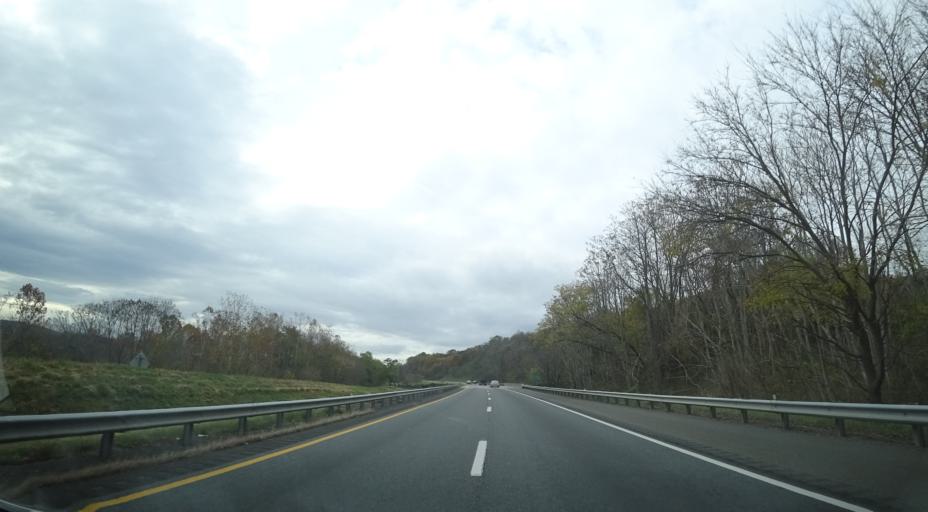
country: US
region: Virginia
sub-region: Fauquier County
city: Marshall
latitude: 38.9093
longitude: -77.9729
